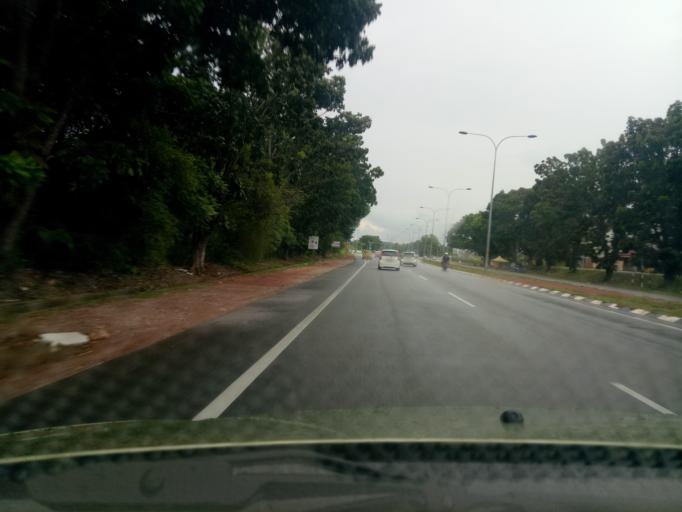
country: MY
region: Kedah
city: Sungai Petani
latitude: 5.6264
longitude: 100.5360
